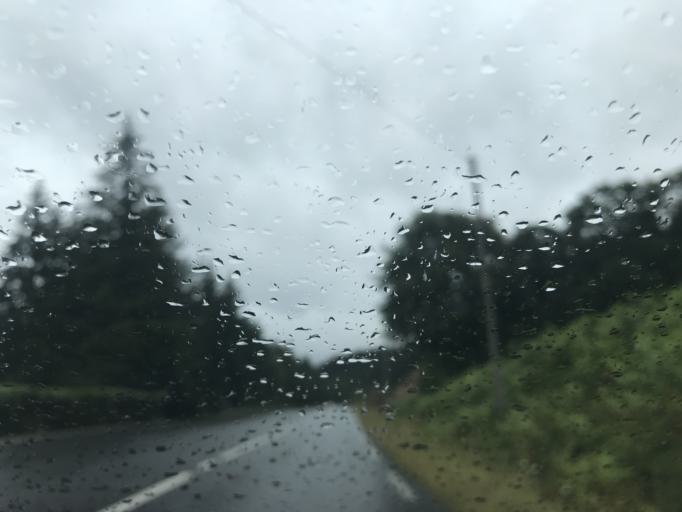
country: FR
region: Auvergne
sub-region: Departement du Puy-de-Dome
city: Job
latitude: 45.6037
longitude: 3.7203
